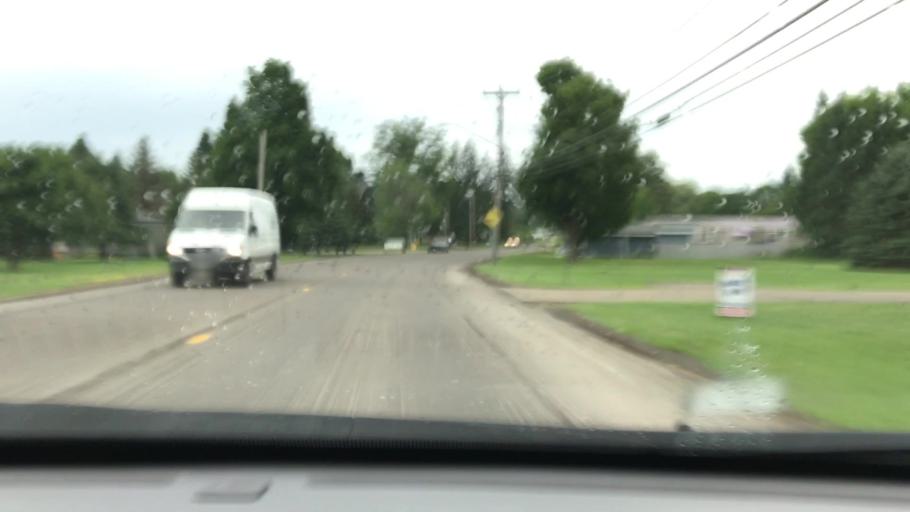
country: US
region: New York
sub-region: Cattaraugus County
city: Salamanca
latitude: 42.2827
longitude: -78.6633
